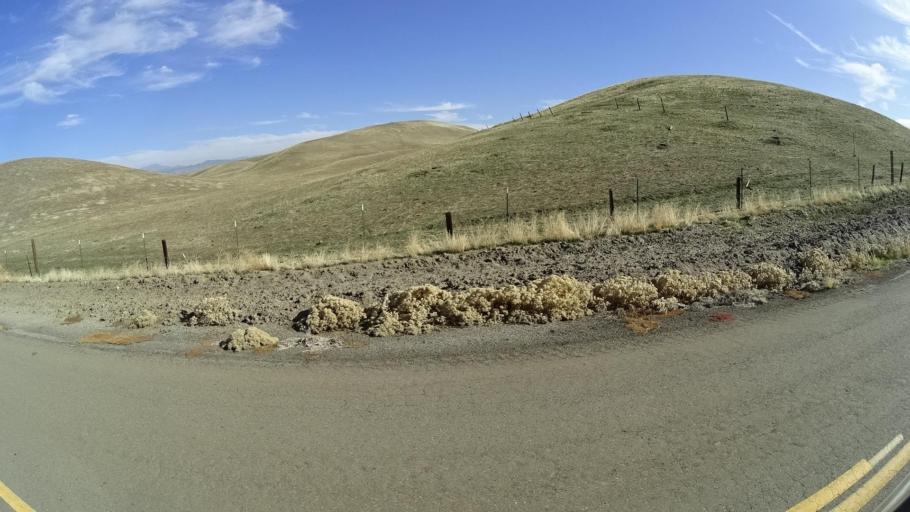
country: US
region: California
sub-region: Kern County
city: Oildale
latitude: 35.6316
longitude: -118.9451
